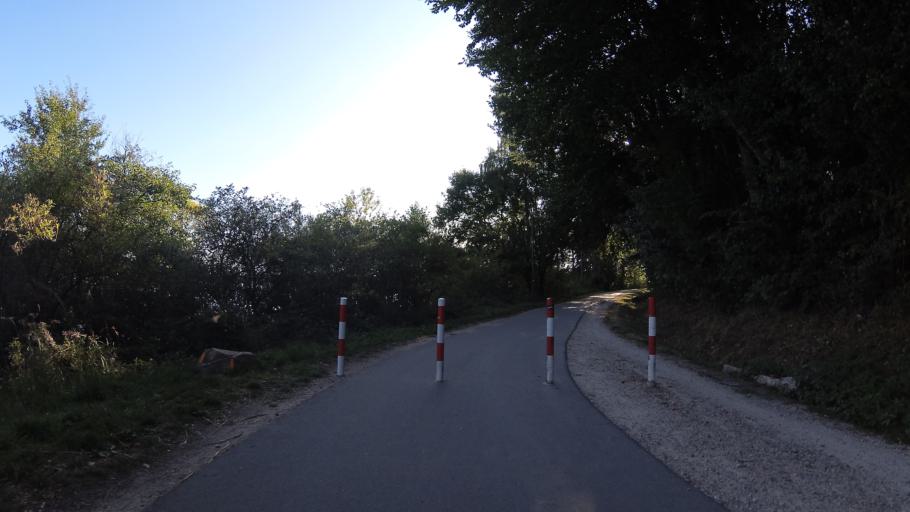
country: DE
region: Rheinland-Pfalz
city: Achtelsbach
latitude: 49.5708
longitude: 7.0725
